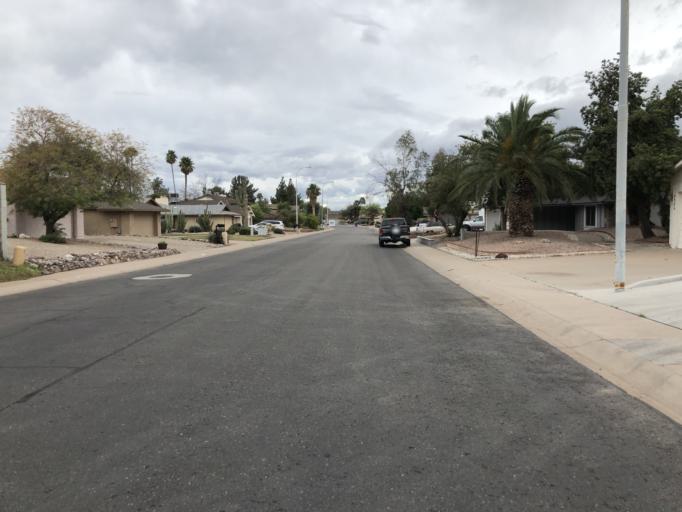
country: US
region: Arizona
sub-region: Maricopa County
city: Chandler
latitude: 33.3041
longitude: -111.9202
